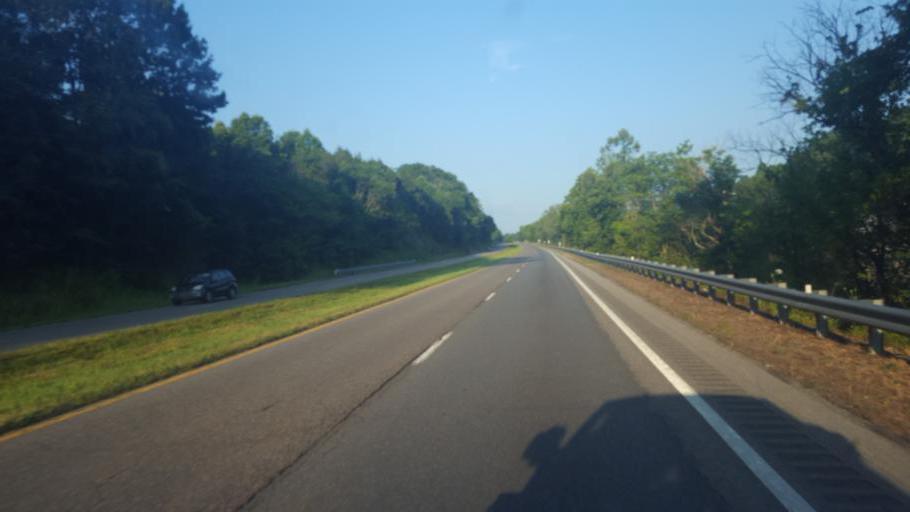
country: US
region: Tennessee
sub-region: Hawkins County
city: Mount Carmel
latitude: 36.6417
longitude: -82.7237
